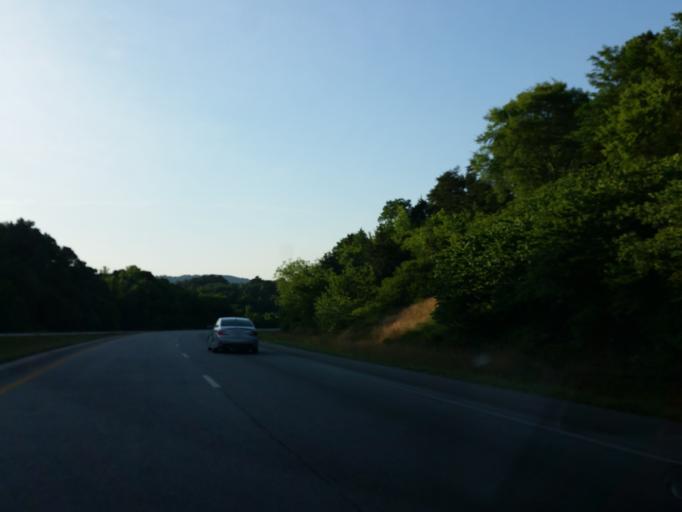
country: US
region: Georgia
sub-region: Dade County
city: Trenton
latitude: 34.7974
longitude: -85.5493
